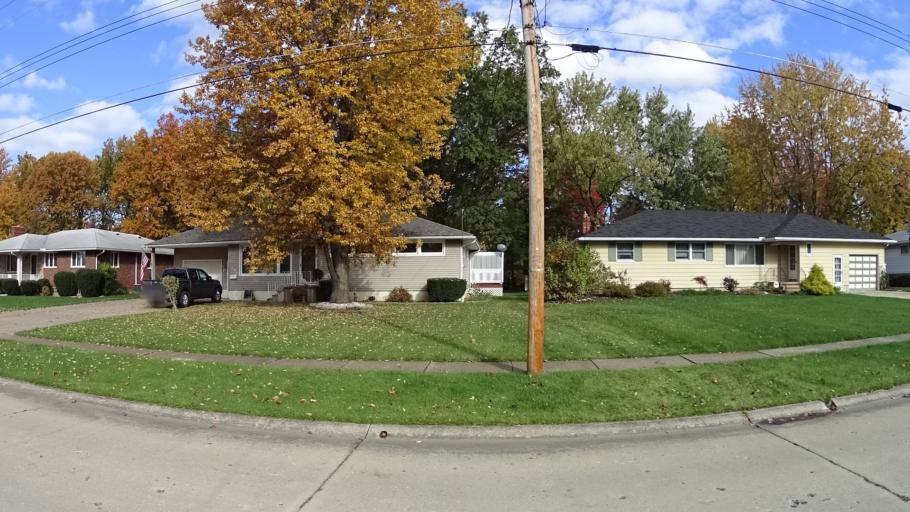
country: US
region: Ohio
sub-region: Lorain County
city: Lorain
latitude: 41.4239
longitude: -82.1919
